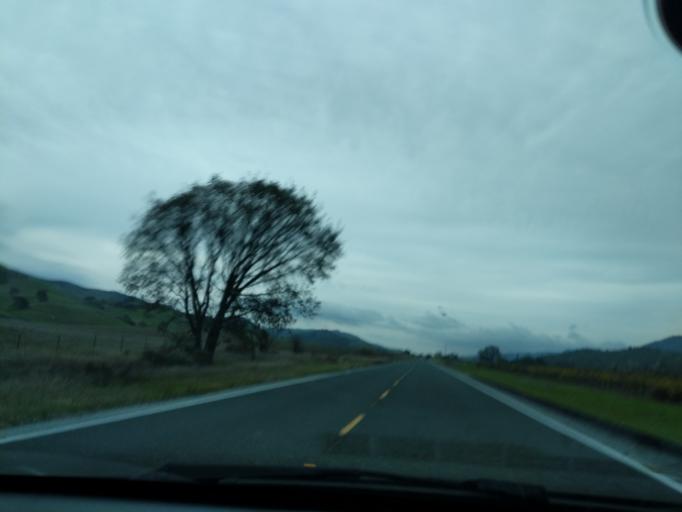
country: US
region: California
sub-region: San Benito County
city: Ridgemark
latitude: 36.6894
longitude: -121.2654
